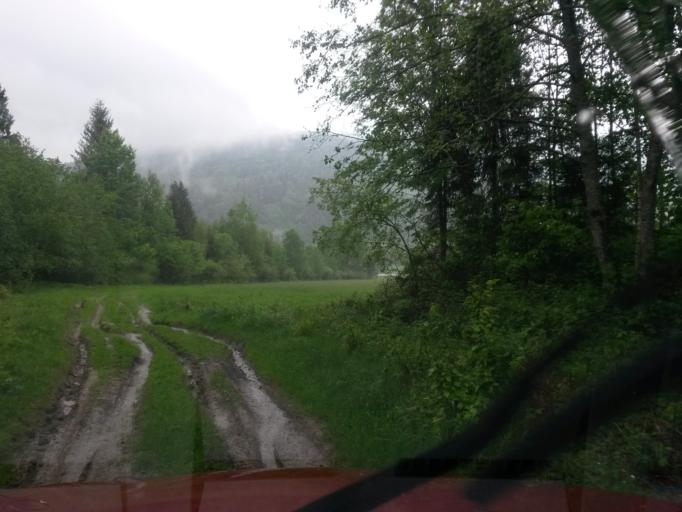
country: SK
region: Kosicky
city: Medzev
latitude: 48.7870
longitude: 20.7757
